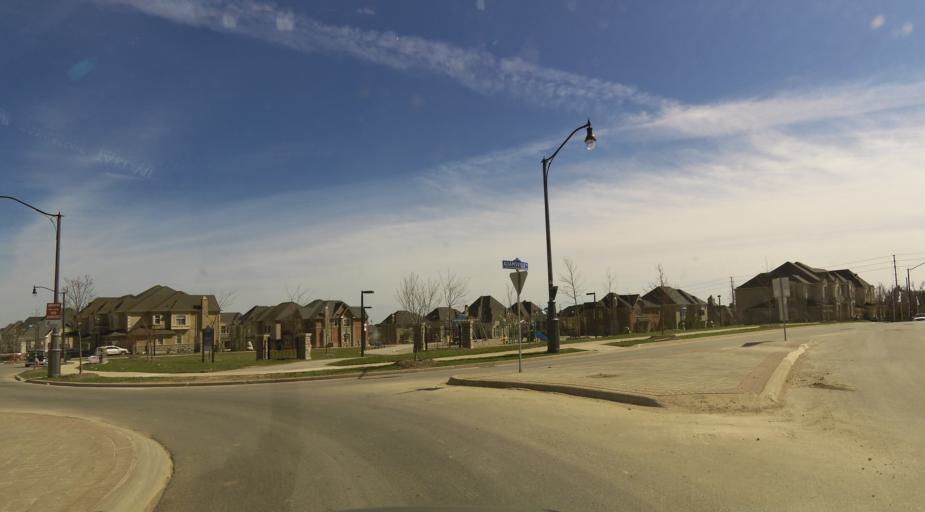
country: CA
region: Ontario
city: Brampton
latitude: 43.6521
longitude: -79.8063
